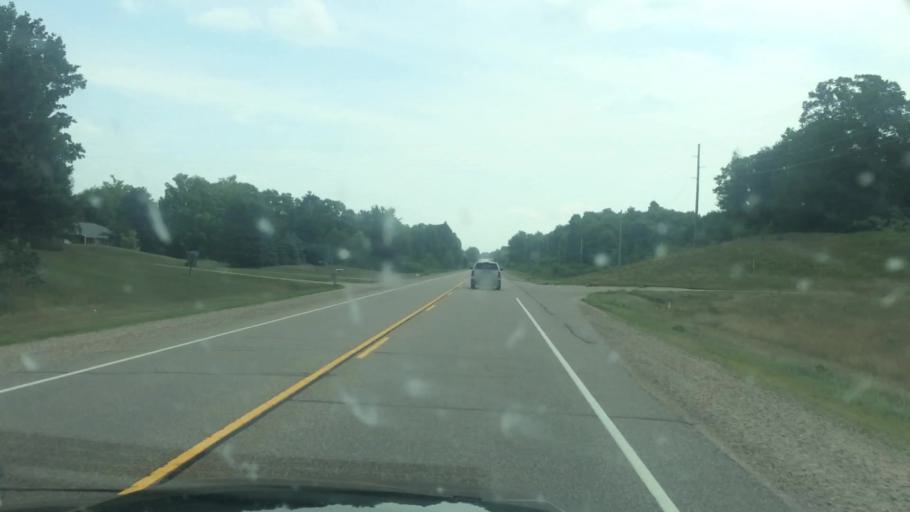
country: US
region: Wisconsin
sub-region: Langlade County
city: Antigo
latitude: 45.1616
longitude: -89.0533
